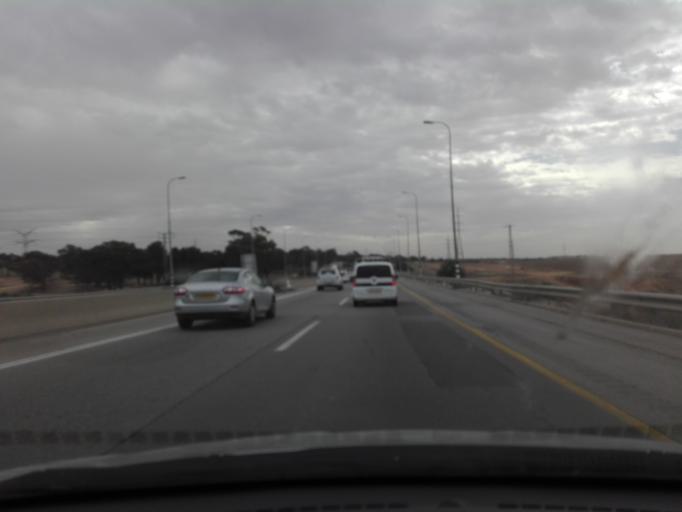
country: IL
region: Southern District
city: Lehavim
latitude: 31.3685
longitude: 34.7948
